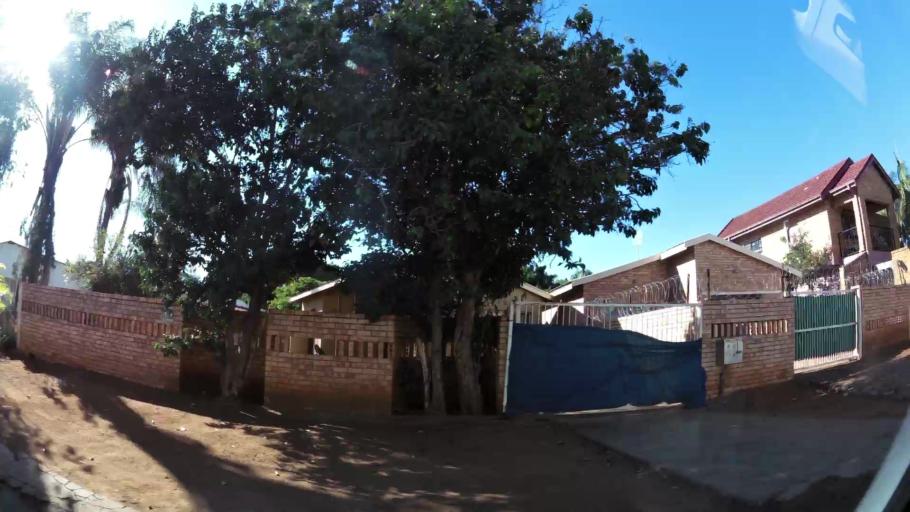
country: ZA
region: Limpopo
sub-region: Waterberg District Municipality
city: Mokopane
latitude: -24.1785
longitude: 28.9972
